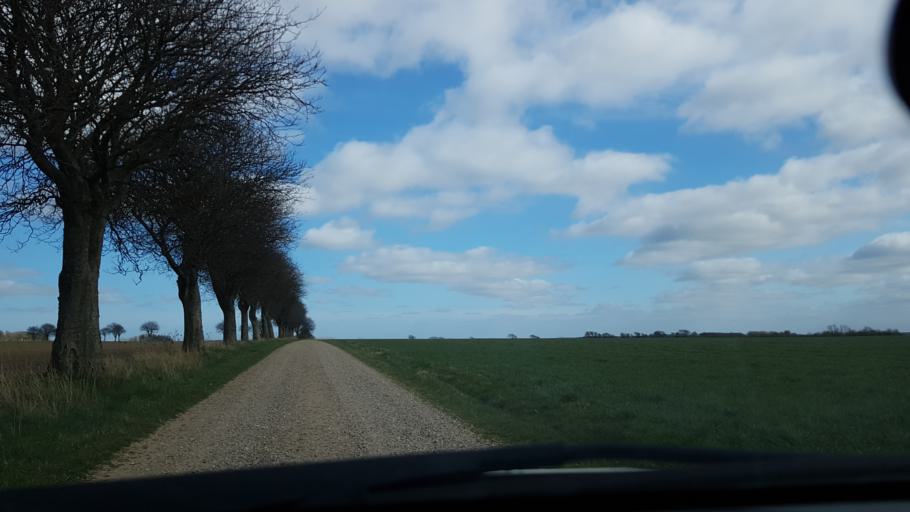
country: DK
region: South Denmark
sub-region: Vejen Kommune
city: Brorup
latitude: 55.4258
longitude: 9.0226
